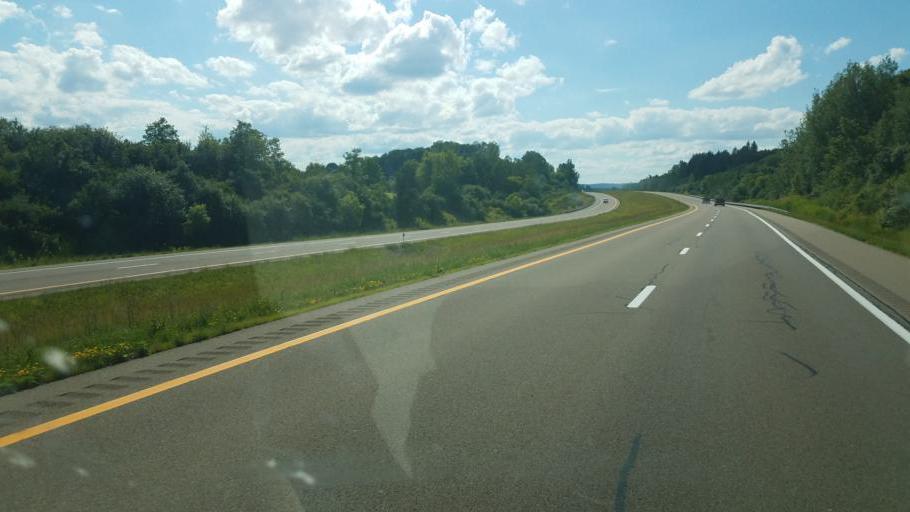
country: US
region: New York
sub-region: Steuben County
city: Hornell
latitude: 42.3730
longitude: -77.6303
